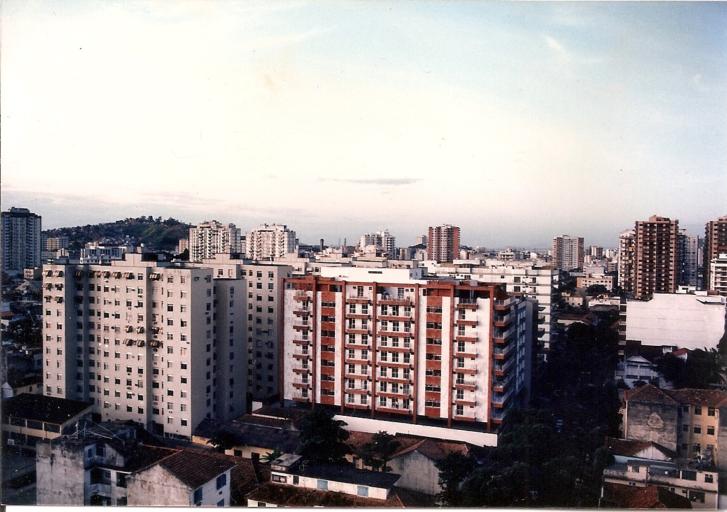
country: BR
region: Rio de Janeiro
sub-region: Rio De Janeiro
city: Rio de Janeiro
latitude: -22.9292
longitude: -43.2323
